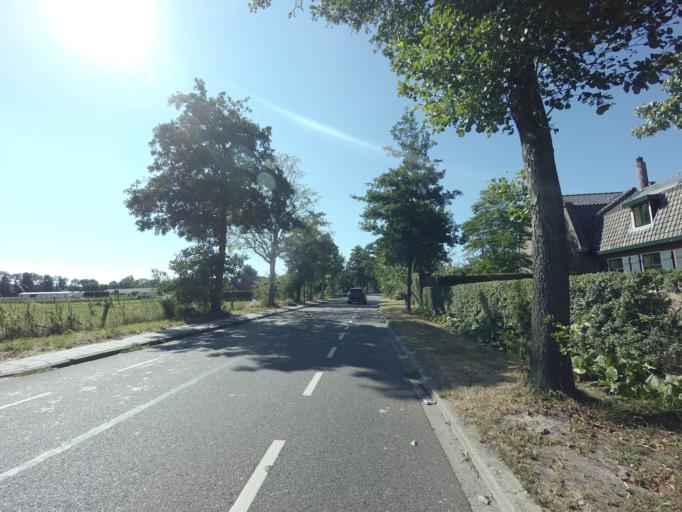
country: NL
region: Utrecht
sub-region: Stichtse Vecht
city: Maarssen
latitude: 52.1434
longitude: 5.0692
